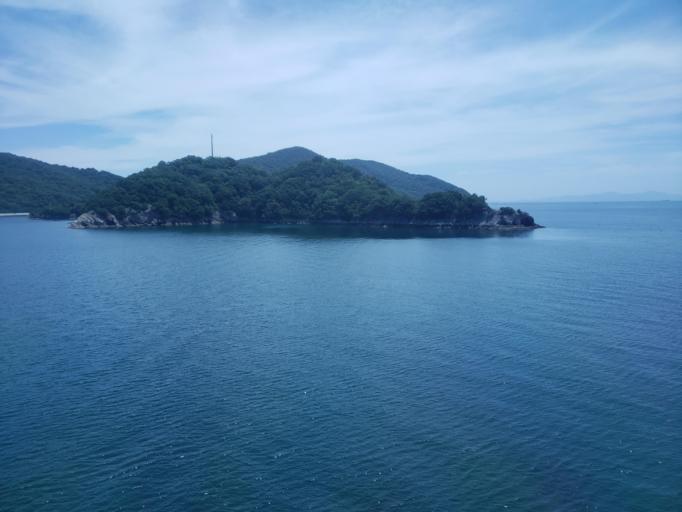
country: JP
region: Kagawa
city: Tonosho
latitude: 34.4479
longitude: 134.3175
